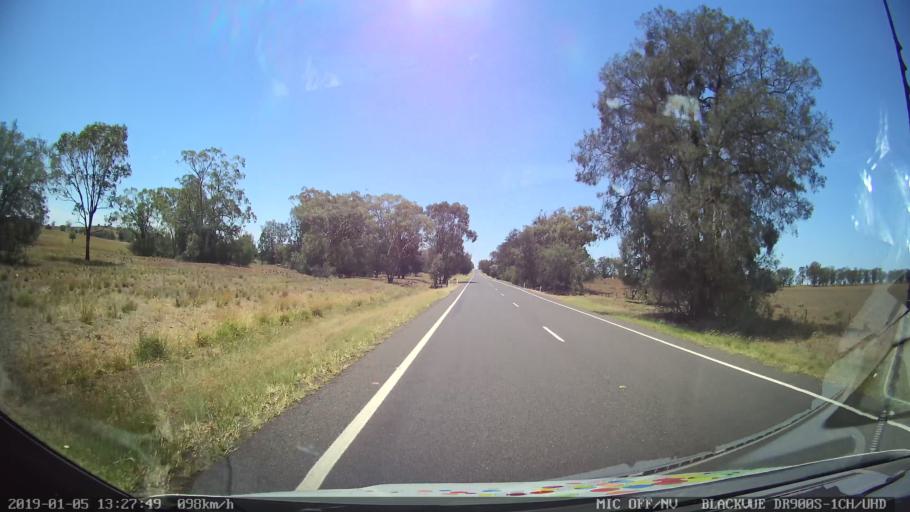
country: AU
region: New South Wales
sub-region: Gunnedah
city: Gunnedah
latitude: -31.0413
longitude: 150.0345
